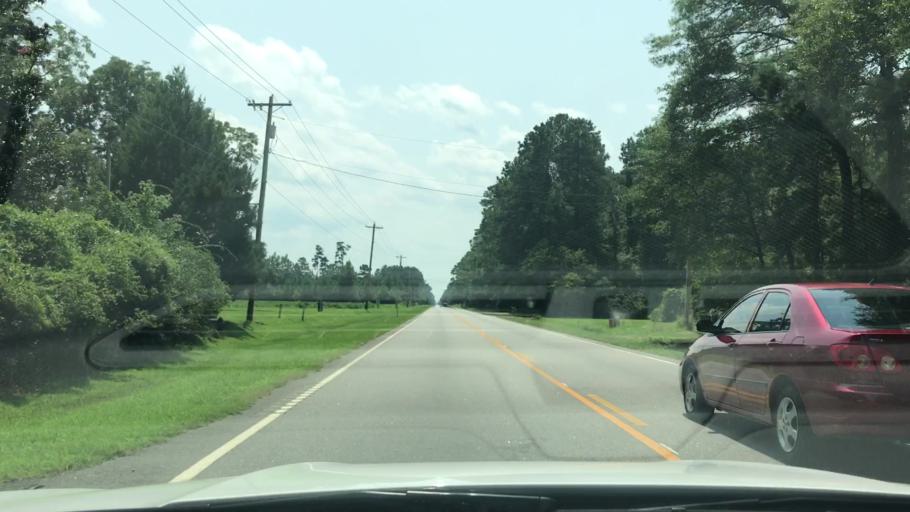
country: US
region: South Carolina
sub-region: Horry County
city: Conway
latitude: 33.7681
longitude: -79.0726
